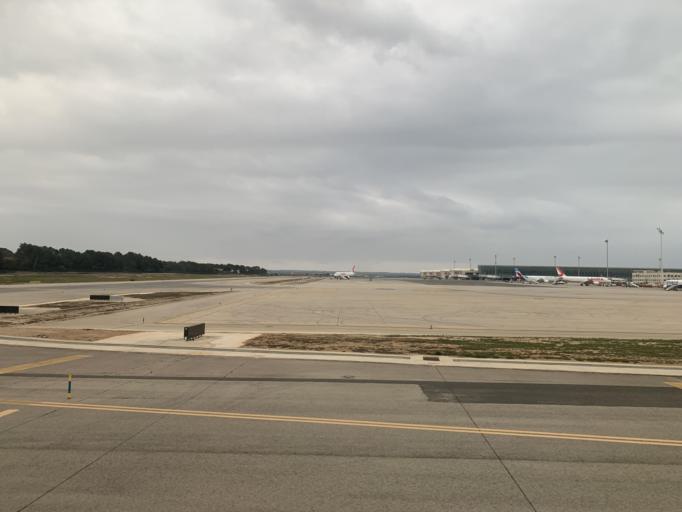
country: ES
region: Balearic Islands
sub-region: Illes Balears
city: s'Arenal
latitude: 39.5568
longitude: 2.7330
